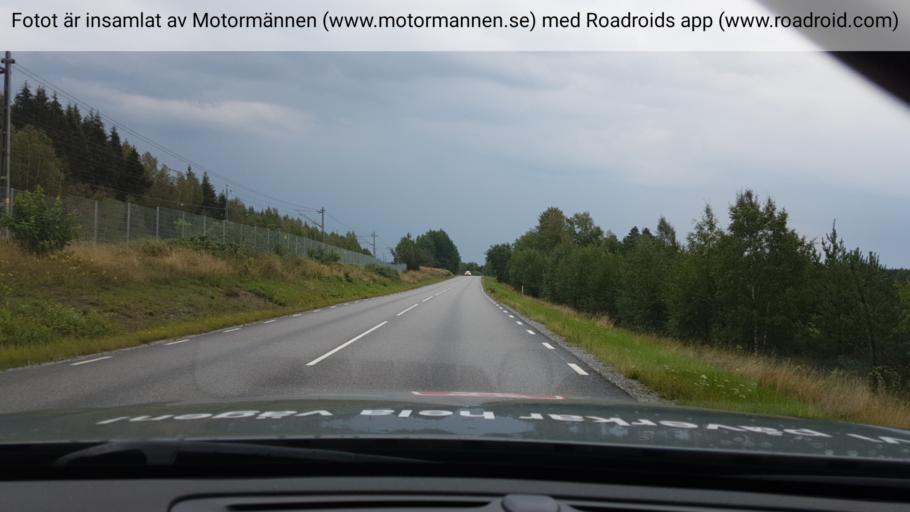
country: SE
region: Uppsala
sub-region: Habo Kommun
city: Balsta
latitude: 59.5327
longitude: 17.5750
